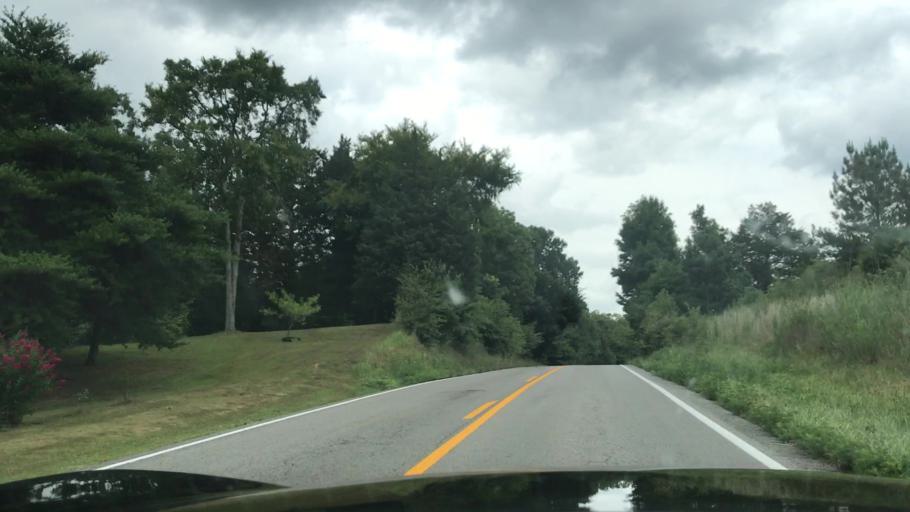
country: US
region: Kentucky
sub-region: Muhlenberg County
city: Central City
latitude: 37.2040
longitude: -86.9539
